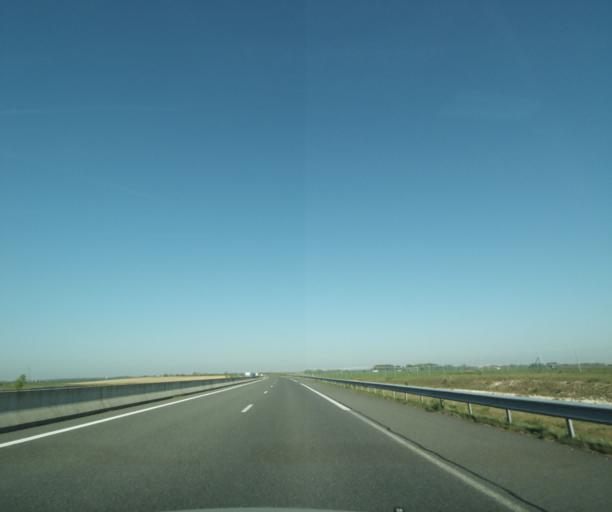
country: FR
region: Centre
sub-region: Departement du Loiret
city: Pannes
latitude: 48.0767
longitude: 2.6293
